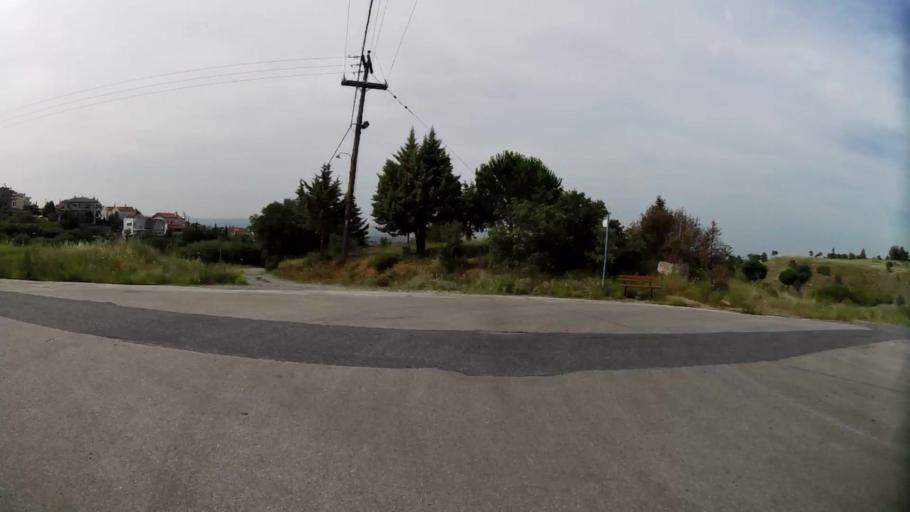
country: GR
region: Central Macedonia
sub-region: Nomos Thessalonikis
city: Panorama
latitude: 40.5780
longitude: 23.0062
